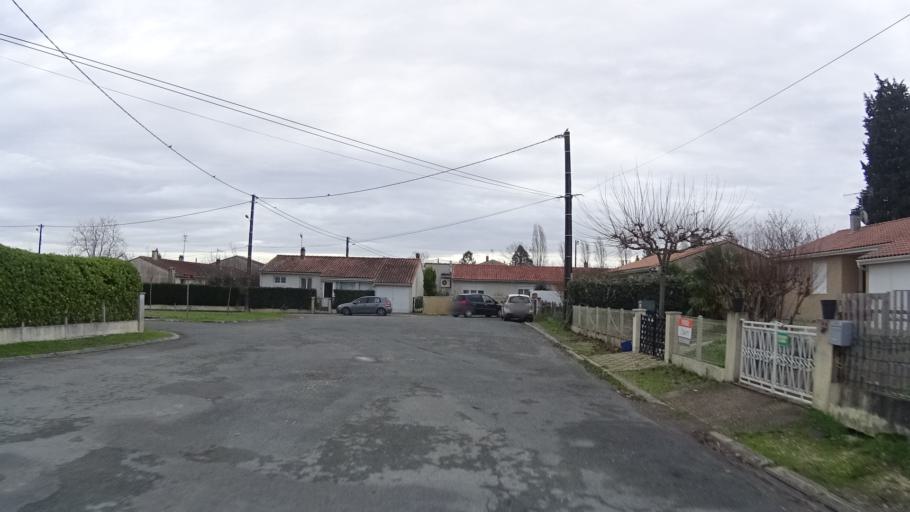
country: FR
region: Aquitaine
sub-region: Departement de la Dordogne
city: Saint-Aulaye
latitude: 45.2034
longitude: 0.1308
